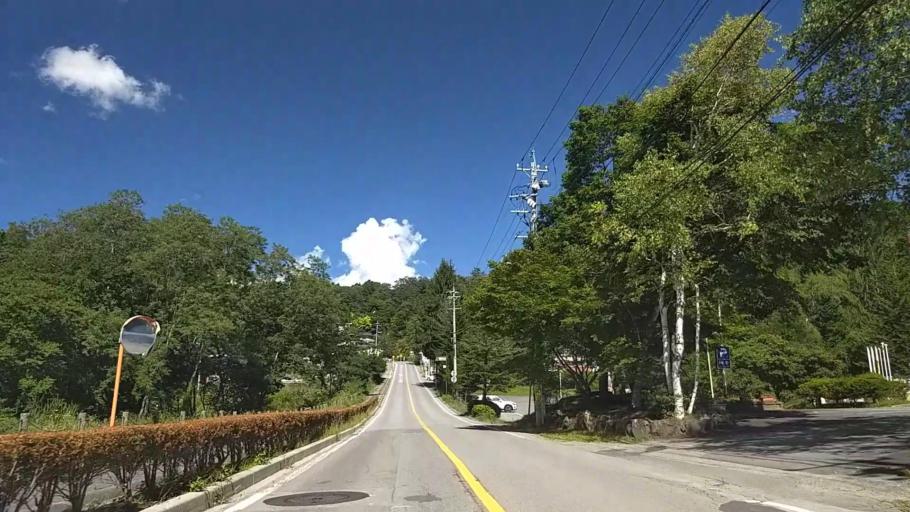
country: JP
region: Nagano
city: Chino
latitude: 36.0531
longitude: 138.2605
